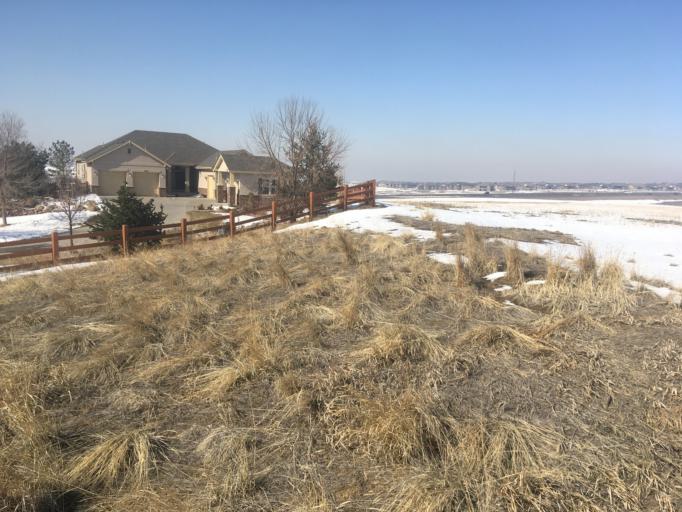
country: US
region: Colorado
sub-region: Boulder County
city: Lafayette
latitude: 39.9736
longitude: -105.0529
